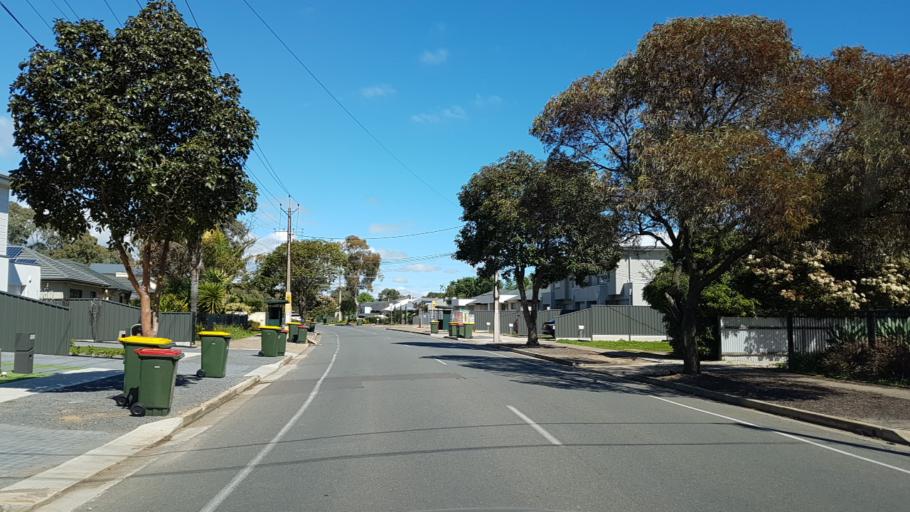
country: AU
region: South Australia
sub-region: Marion
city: Plympton Park
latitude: -34.9906
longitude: 138.5470
